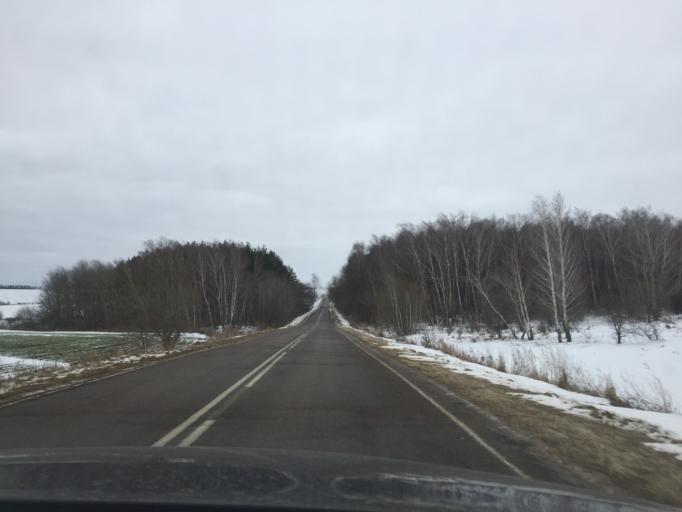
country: RU
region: Tula
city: Shchekino
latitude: 53.8109
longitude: 37.5410
